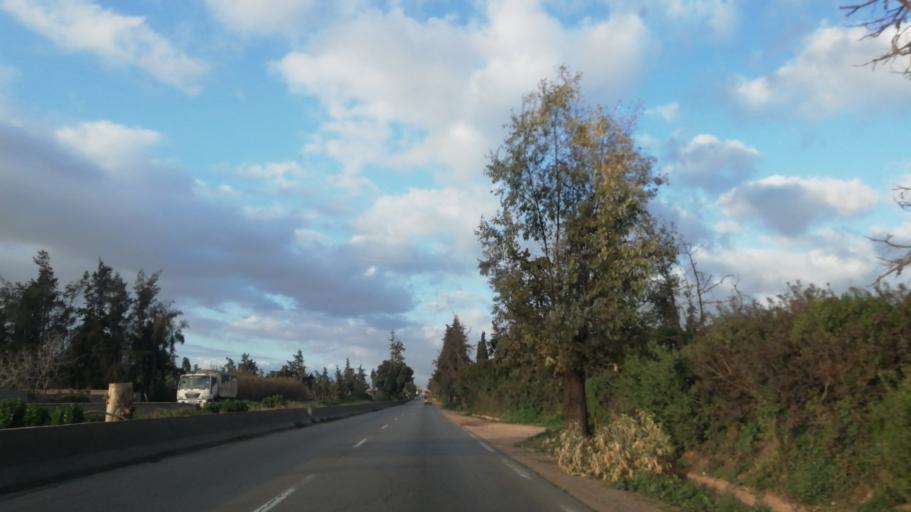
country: DZ
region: Oran
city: Bou Tlelis
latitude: 35.5952
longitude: -0.7863
